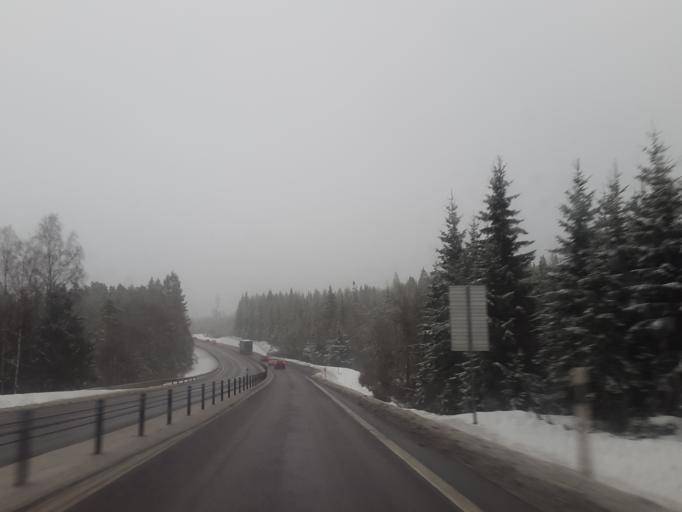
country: SE
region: Joenkoeping
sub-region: Jonkopings Kommun
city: Taberg
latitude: 57.7510
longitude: 13.9701
